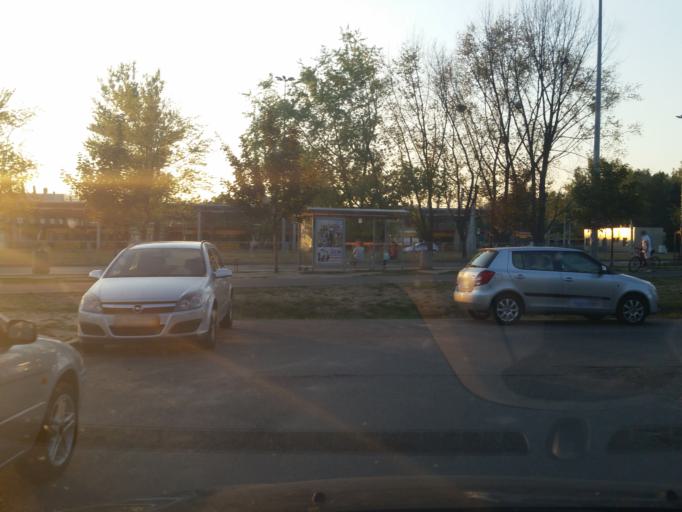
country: PL
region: Masovian Voivodeship
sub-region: Warszawa
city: Bielany
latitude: 52.2911
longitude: 20.9312
